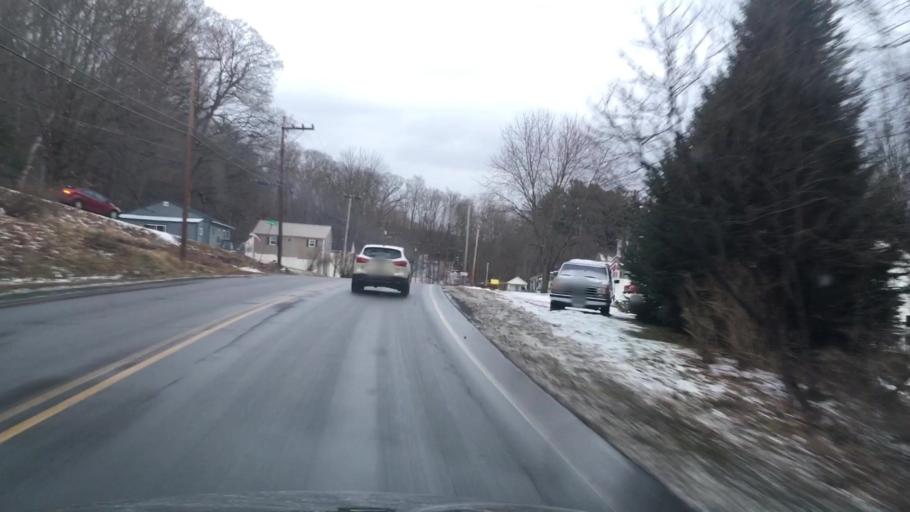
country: US
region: New Hampshire
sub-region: Sullivan County
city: Claremont
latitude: 43.3922
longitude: -72.3702
